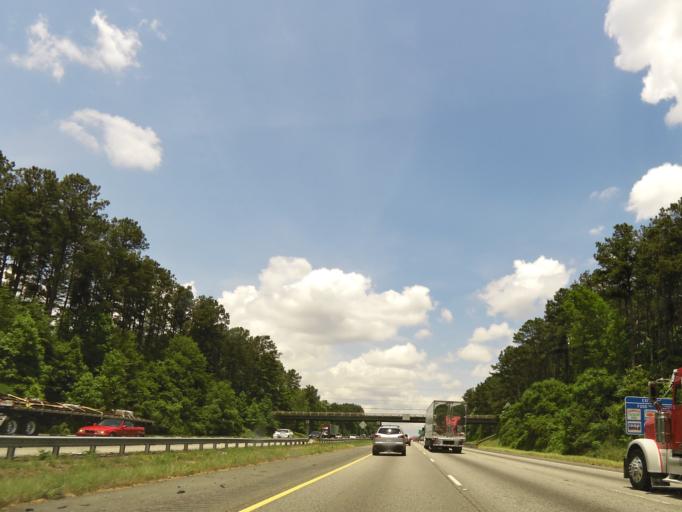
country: US
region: Georgia
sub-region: Henry County
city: Locust Grove
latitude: 33.3295
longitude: -84.1219
